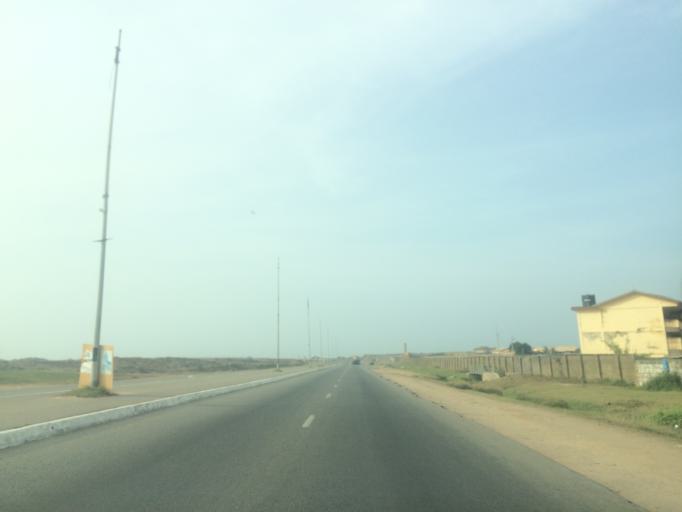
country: GH
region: Greater Accra
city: Accra
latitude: 5.5346
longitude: -0.2215
